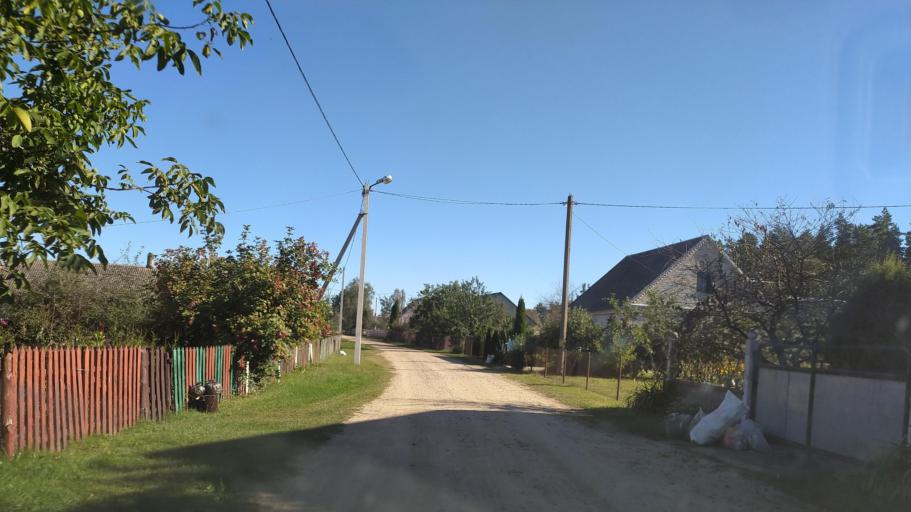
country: BY
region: Brest
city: Pruzhany
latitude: 52.4832
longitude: 24.7082
